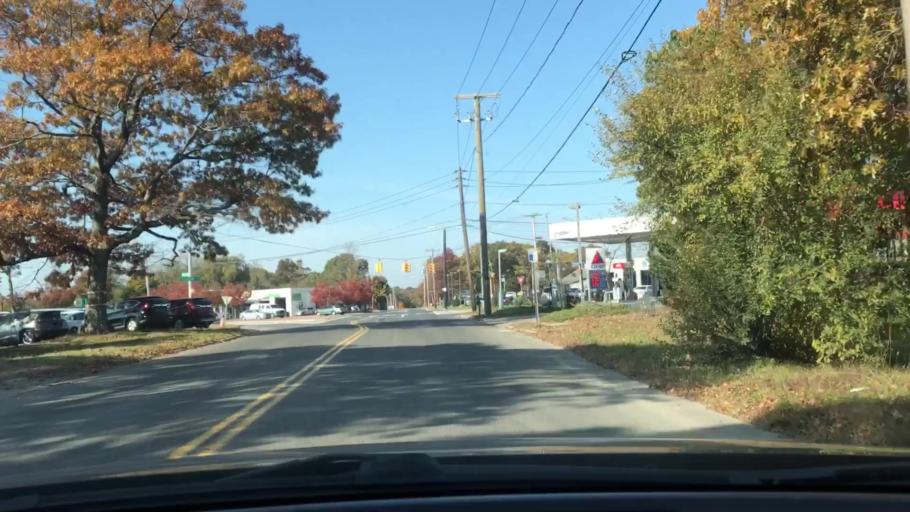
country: US
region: New York
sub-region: Suffolk County
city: Riverhead
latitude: 40.9280
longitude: -72.6840
